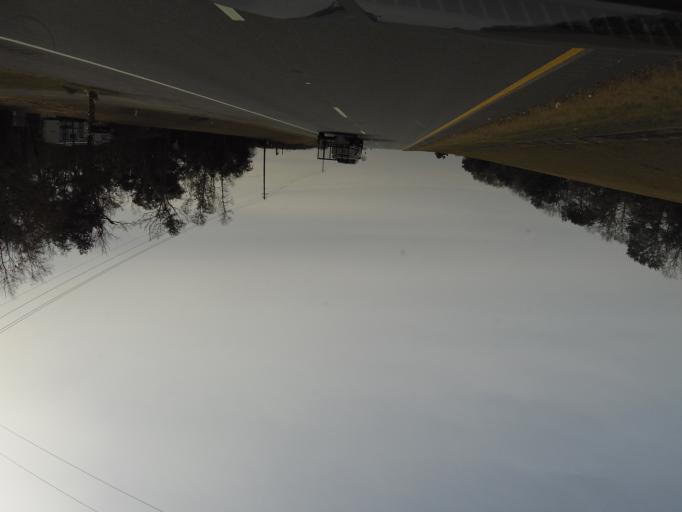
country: US
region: Georgia
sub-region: Seminole County
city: Donalsonville
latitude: 31.0973
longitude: -85.0047
